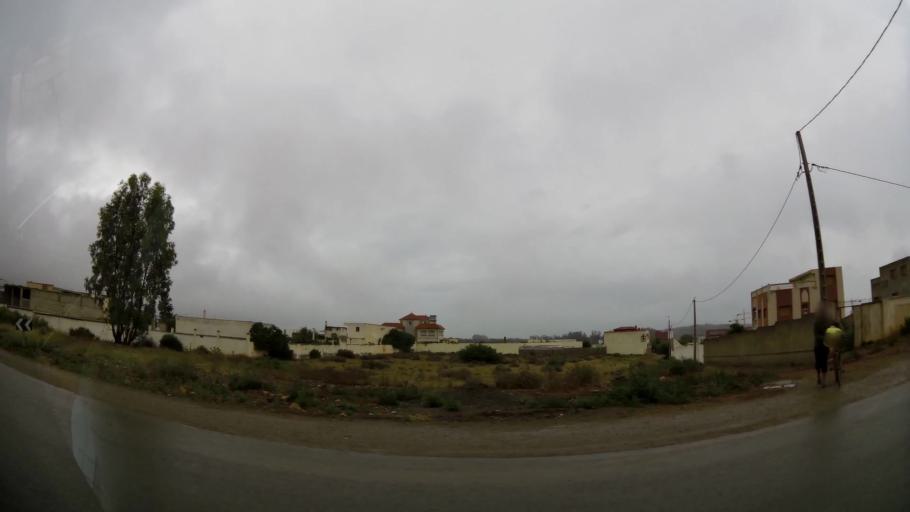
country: MA
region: Taza-Al Hoceima-Taounate
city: Imzourene
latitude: 35.1937
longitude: -3.8920
